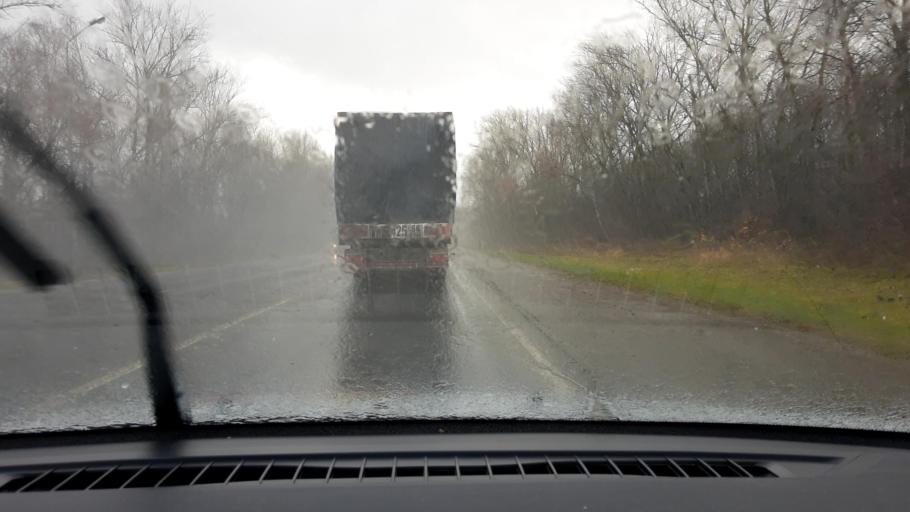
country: RU
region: Nizjnij Novgorod
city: Pamyat' Parizhskoy Kommuny
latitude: 56.0409
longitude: 44.4590
